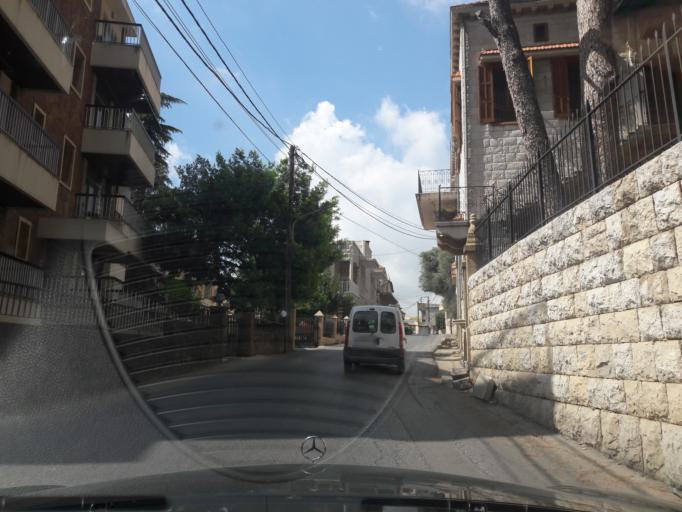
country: LB
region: Mont-Liban
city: Djounie
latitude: 33.9271
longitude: 35.6694
